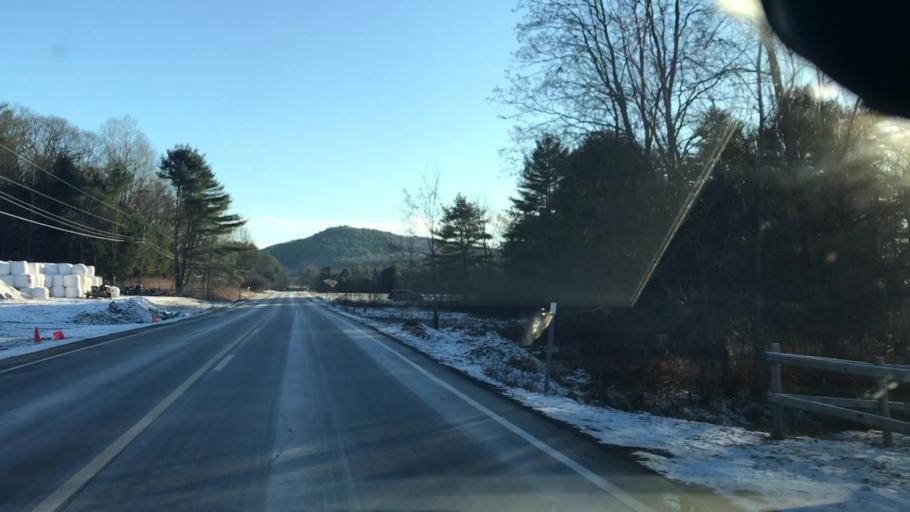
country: US
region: New Hampshire
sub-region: Grafton County
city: Lyme Town Offices
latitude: 43.8546
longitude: -72.1557
